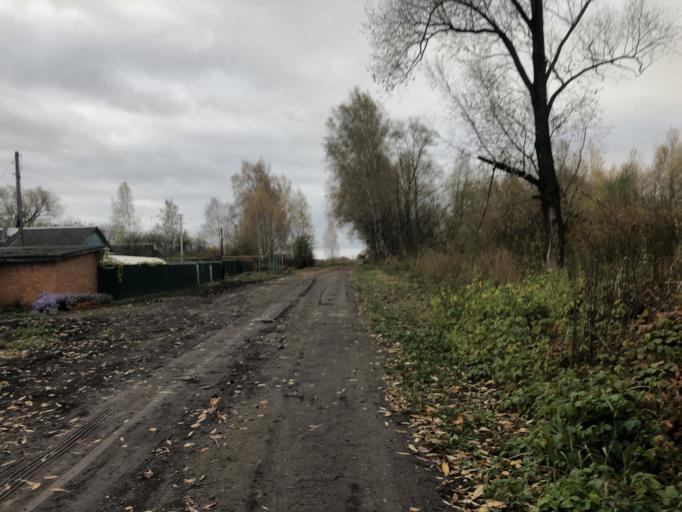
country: RU
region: Tula
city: Kimovsk
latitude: 53.9561
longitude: 38.7856
